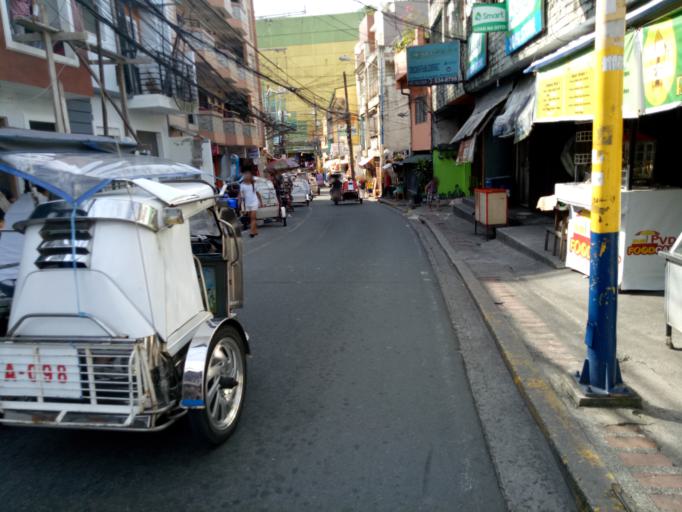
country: PH
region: Metro Manila
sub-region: San Juan
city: San Juan
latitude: 14.5913
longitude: 121.0265
